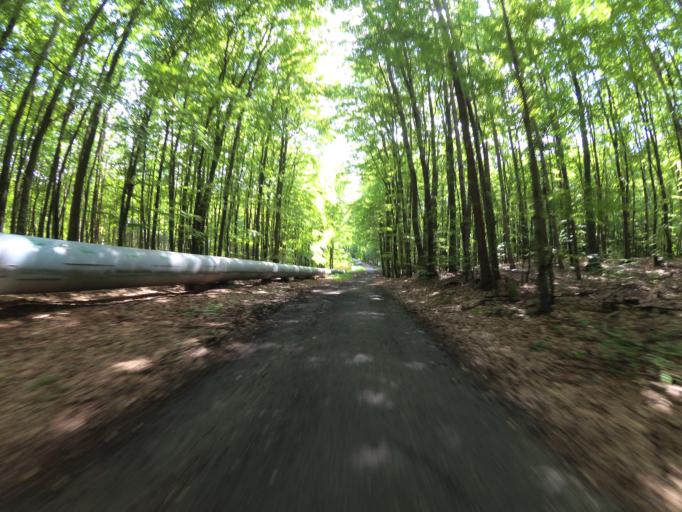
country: PL
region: Pomeranian Voivodeship
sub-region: Gdynia
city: Wielki Kack
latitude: 54.5034
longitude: 18.4930
